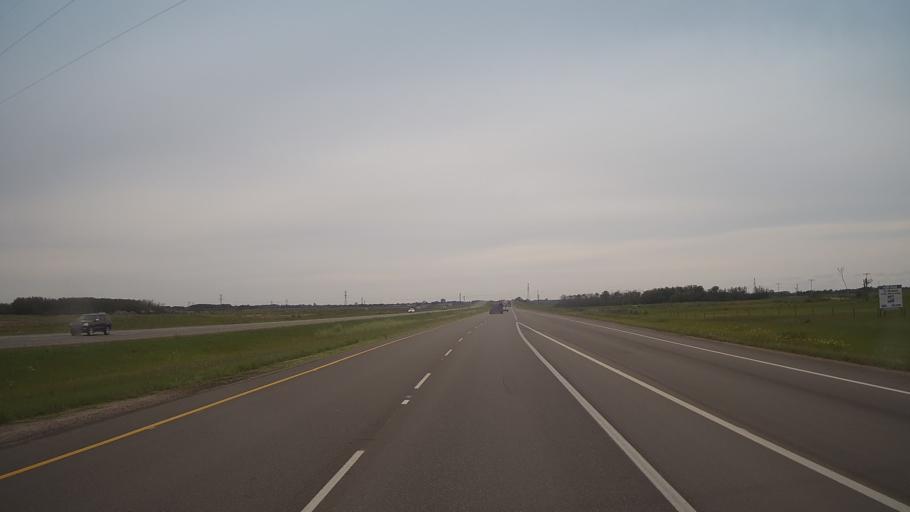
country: CA
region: Saskatchewan
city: Saskatoon
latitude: 52.0595
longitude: -106.6002
